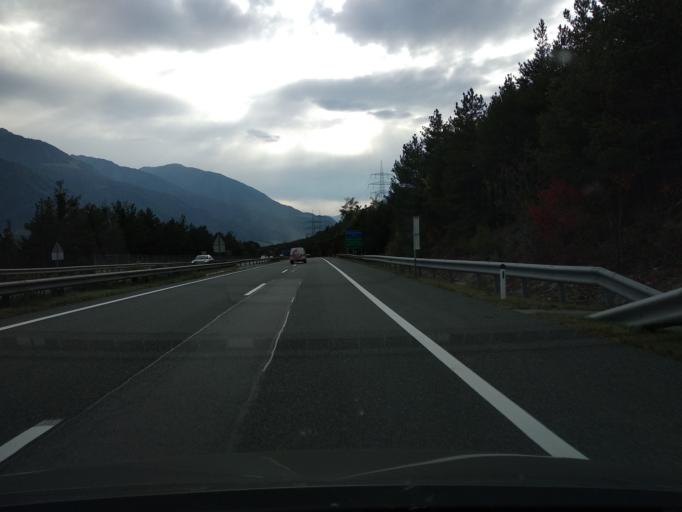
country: AT
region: Tyrol
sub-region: Politischer Bezirk Imst
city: Haiming
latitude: 47.2460
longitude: 10.8535
